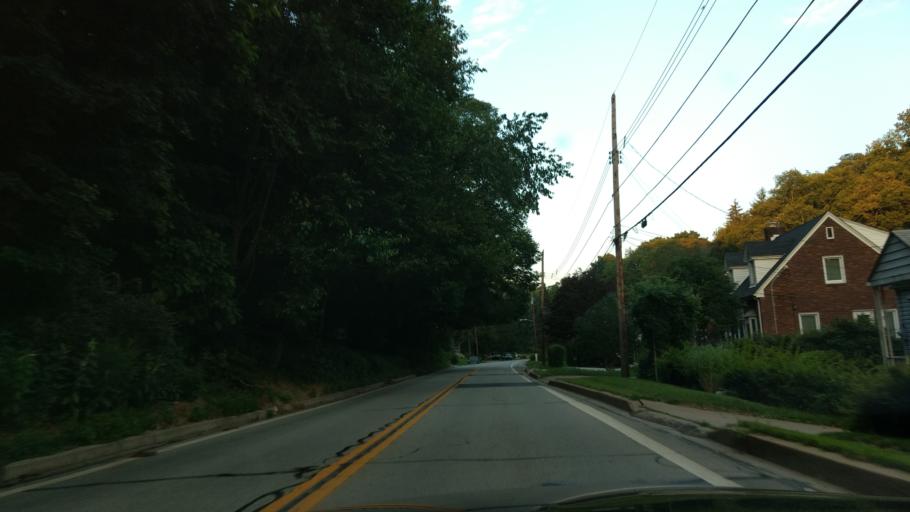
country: US
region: Pennsylvania
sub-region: Allegheny County
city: West View
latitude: 40.5207
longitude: -80.0241
